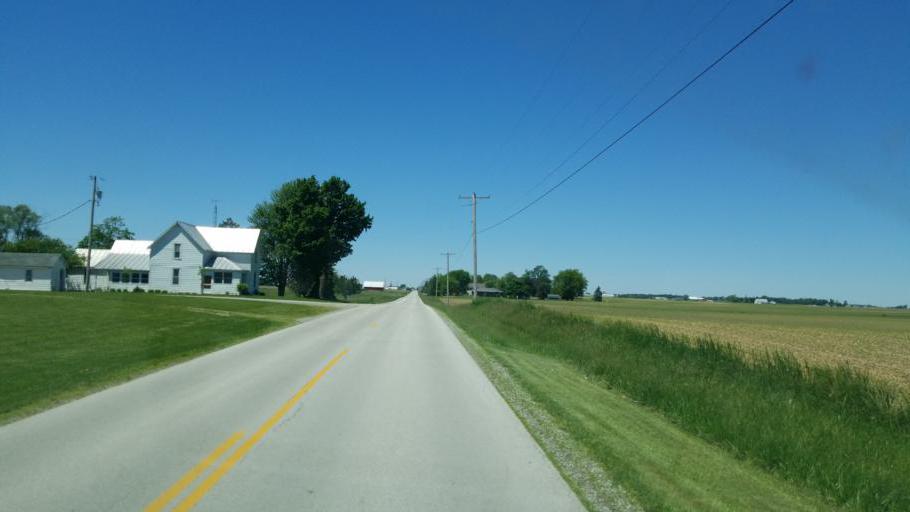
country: US
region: Ohio
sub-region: Auglaize County
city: Minster
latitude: 40.3856
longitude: -84.4081
